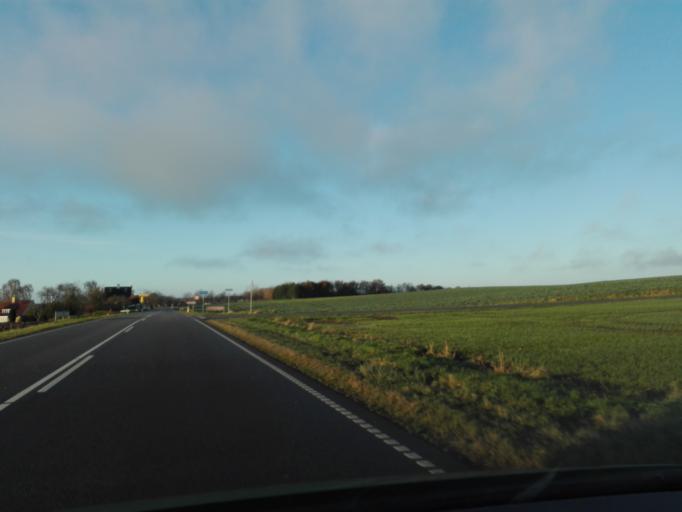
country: DK
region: Central Jutland
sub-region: Skanderborg Kommune
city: Skanderborg
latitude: 56.0637
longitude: 9.9001
